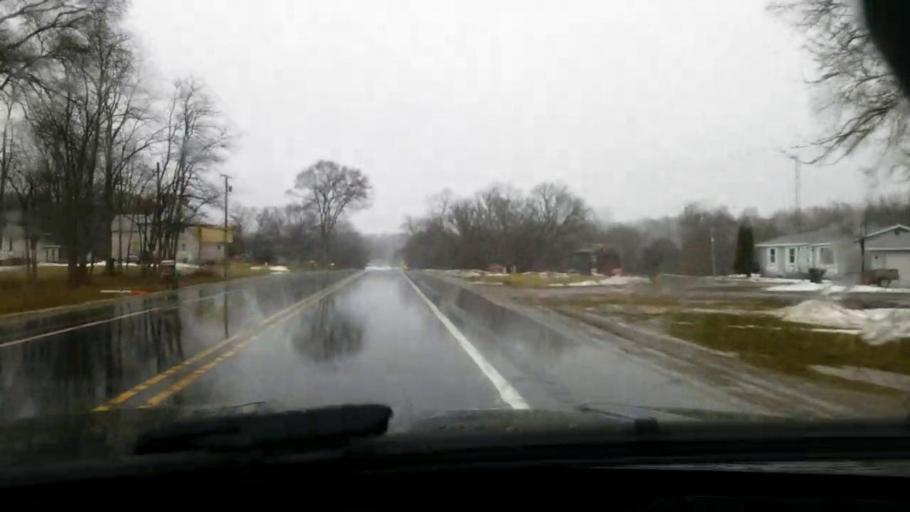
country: US
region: Michigan
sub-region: Jackson County
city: Michigan Center
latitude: 42.1874
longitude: -84.3049
